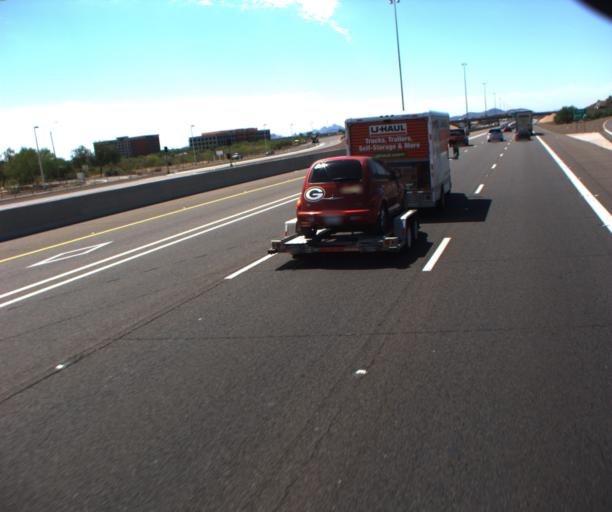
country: US
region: Arizona
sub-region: Maricopa County
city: Anthem
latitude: 33.7038
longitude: -112.1157
